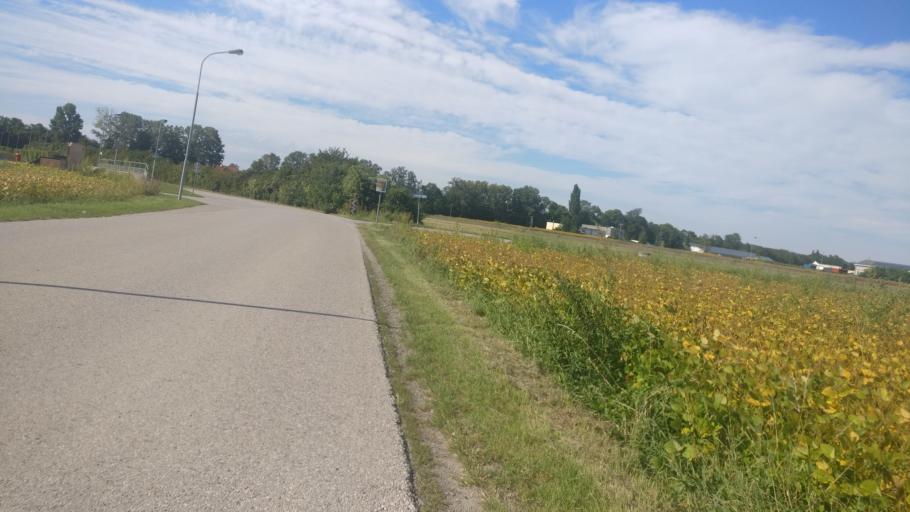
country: AT
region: Lower Austria
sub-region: Politischer Bezirk Baden
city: Ebreichsdorf
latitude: 47.9692
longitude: 16.4129
